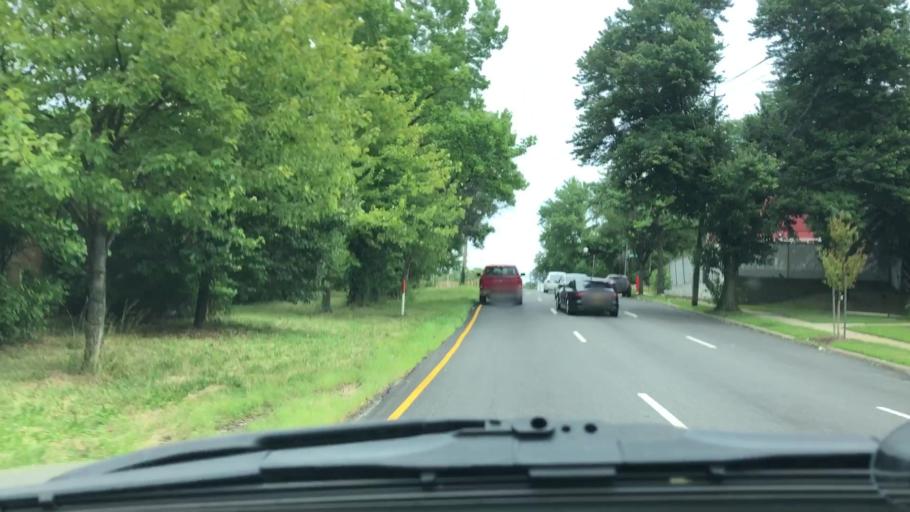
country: US
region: New Jersey
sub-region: Hudson County
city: Bayonne
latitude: 40.6070
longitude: -74.0868
